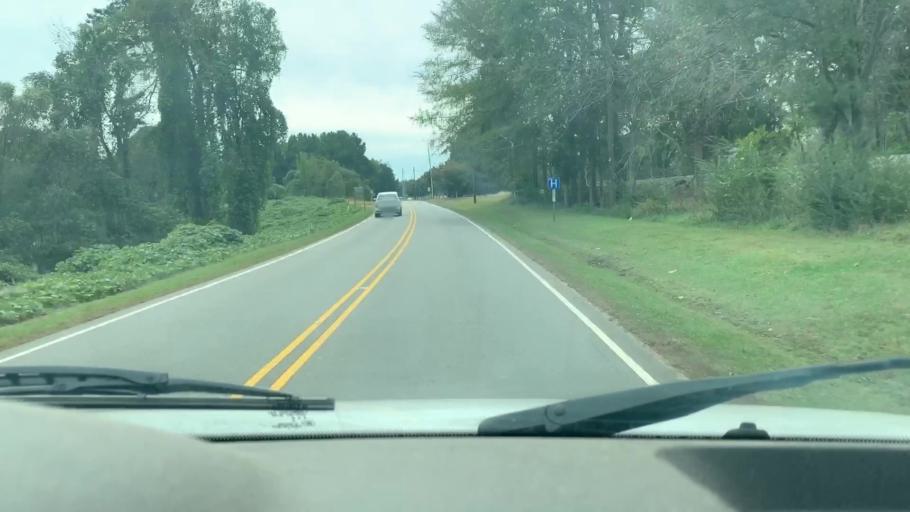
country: US
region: North Carolina
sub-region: Iredell County
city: Mooresville
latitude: 35.5701
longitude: -80.8270
